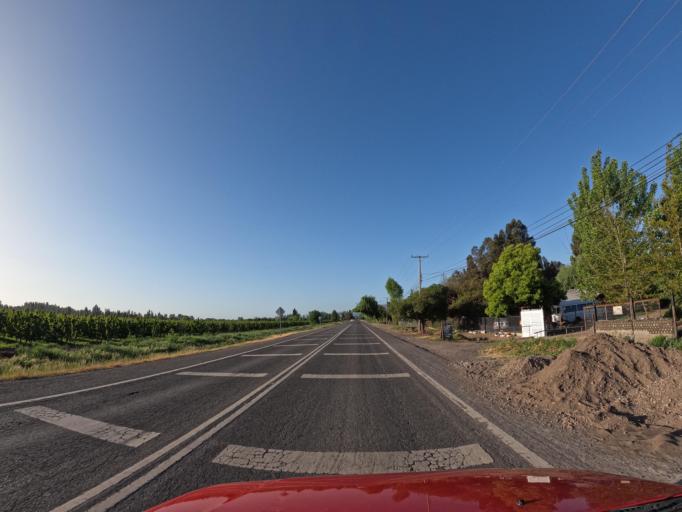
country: CL
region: O'Higgins
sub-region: Provincia de Colchagua
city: Santa Cruz
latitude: -34.4921
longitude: -71.3614
